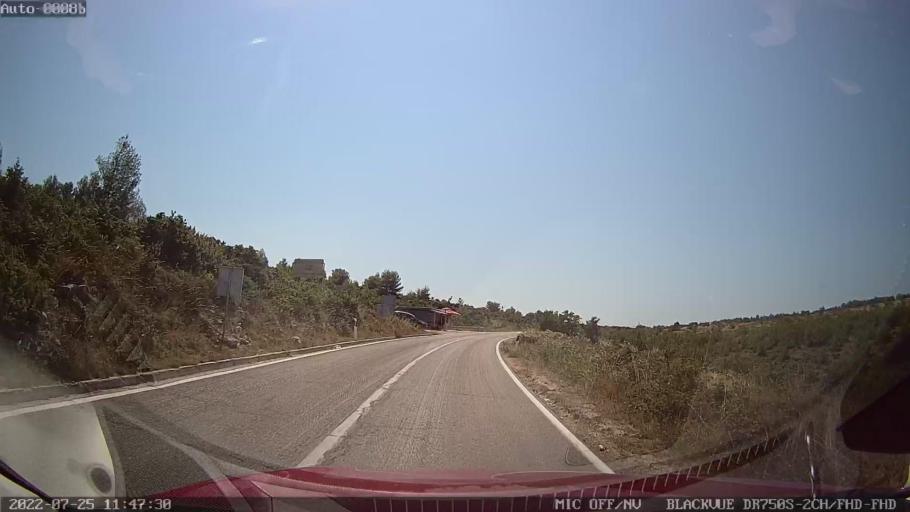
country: HR
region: Zadarska
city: Razanac
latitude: 44.2380
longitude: 15.3019
